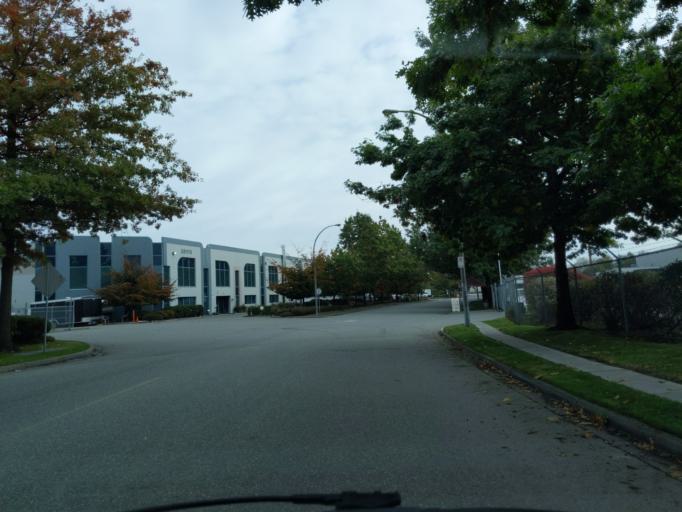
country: CA
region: British Columbia
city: Walnut Grove
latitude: 49.1848
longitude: -122.6635
